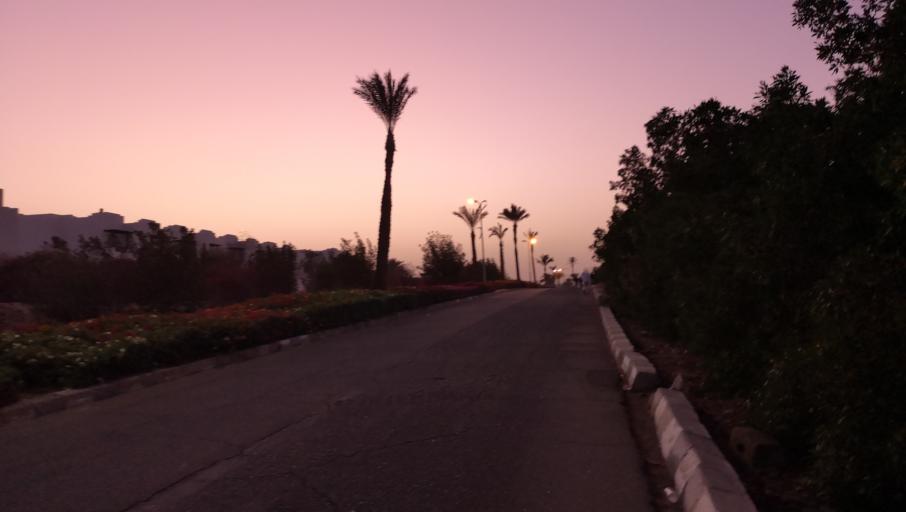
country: EG
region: South Sinai
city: Sharm el-Sheikh
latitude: 27.8623
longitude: 34.3154
